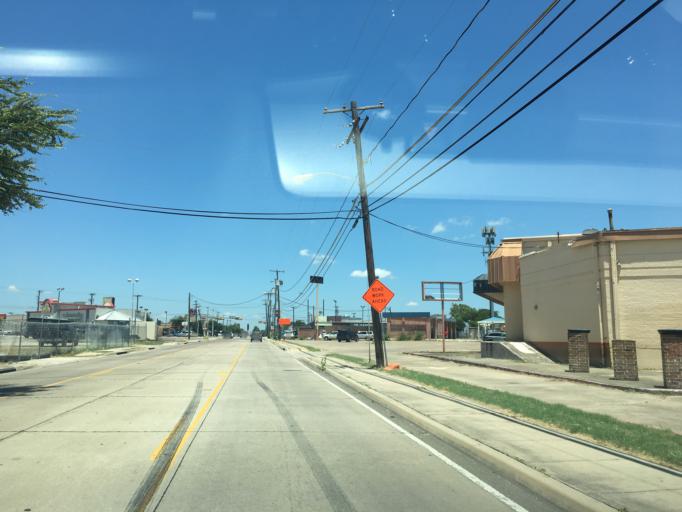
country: US
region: Texas
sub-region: Dallas County
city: Garland
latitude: 32.8474
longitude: -96.6832
